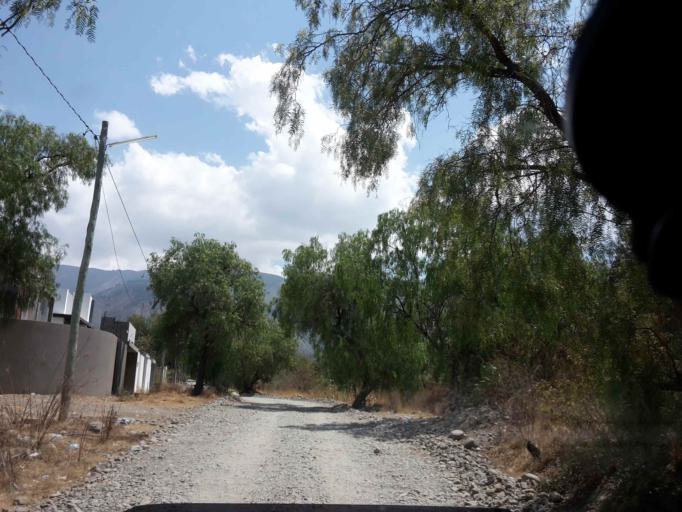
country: BO
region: Cochabamba
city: Cochabamba
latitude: -17.3442
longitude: -66.2124
